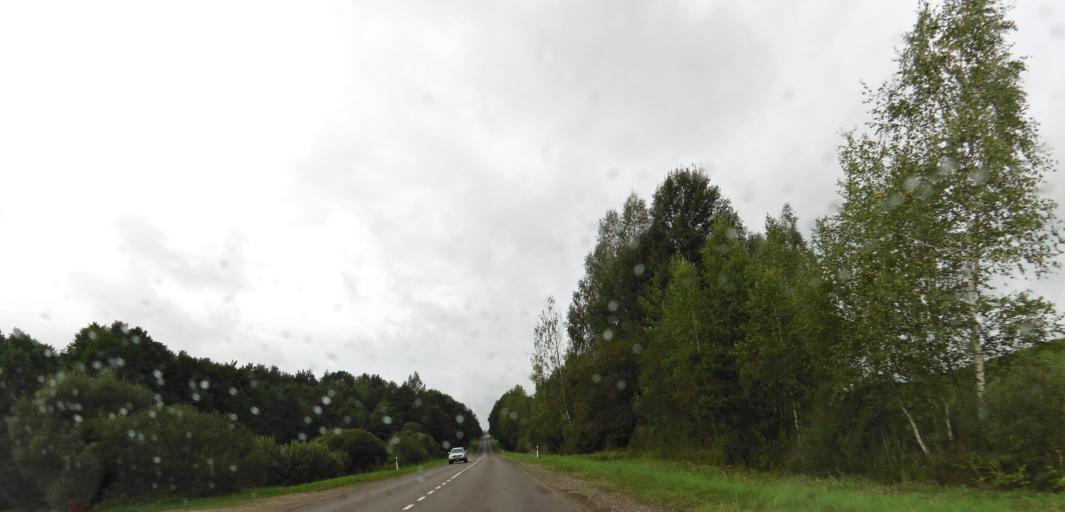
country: LT
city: Moletai
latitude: 55.2139
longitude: 25.3458
